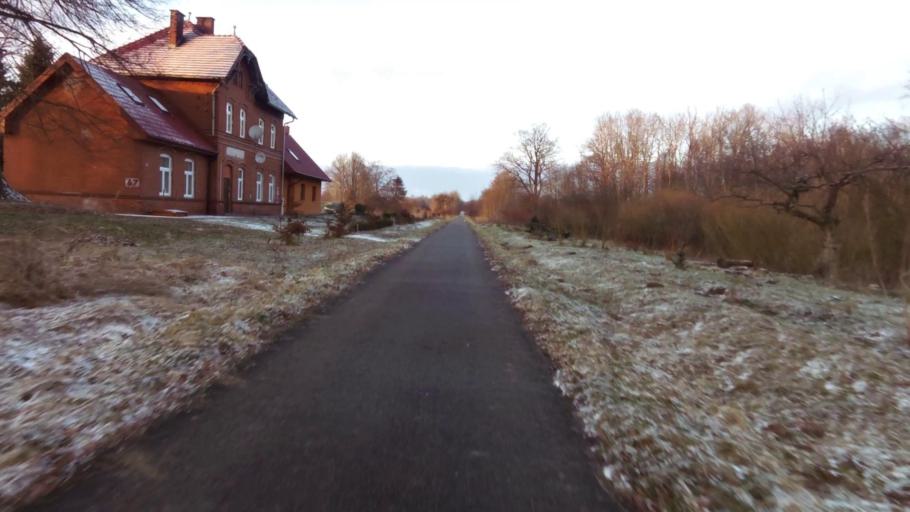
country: PL
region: West Pomeranian Voivodeship
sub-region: Powiat swidwinski
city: Polczyn-Zdroj
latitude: 53.6658
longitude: 16.0295
